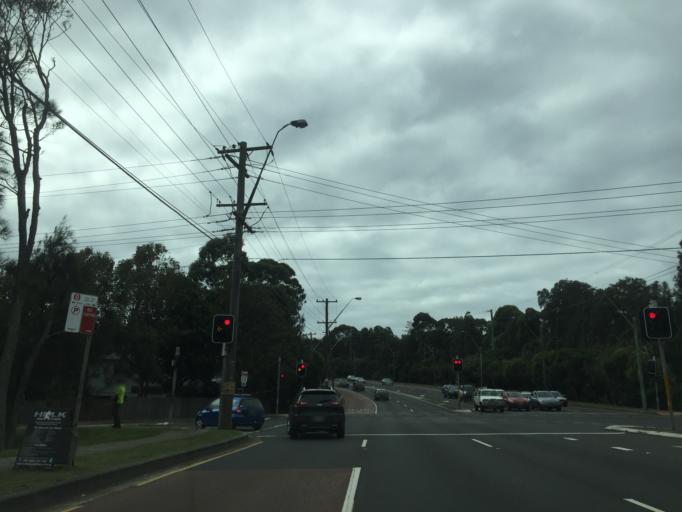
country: AU
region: New South Wales
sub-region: Pittwater
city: Warriewood
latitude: -33.6926
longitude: 151.3043
